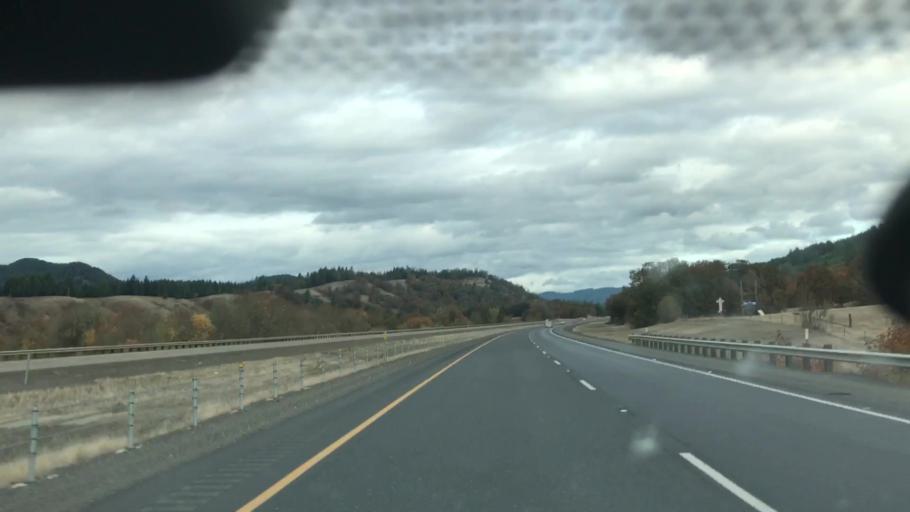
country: US
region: Oregon
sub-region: Douglas County
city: Yoncalla
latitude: 43.5896
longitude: -123.2511
